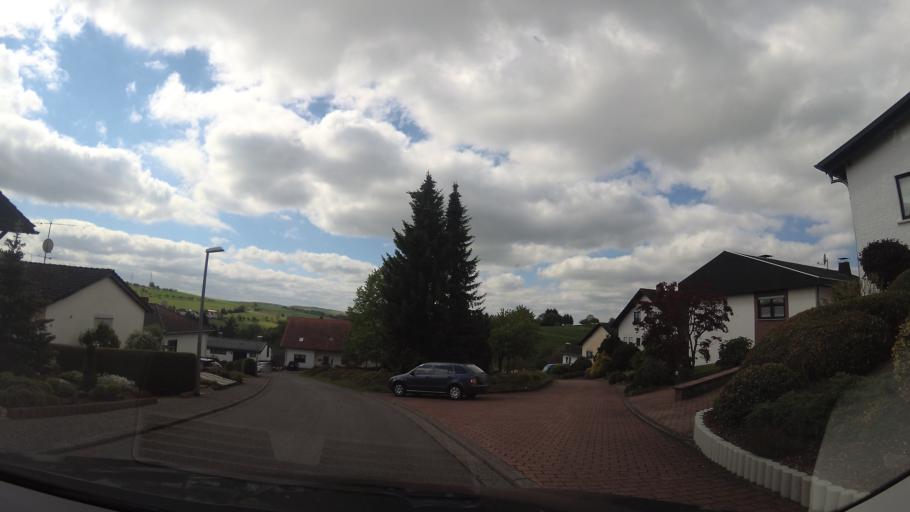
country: DE
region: Saarland
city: Eppelborn
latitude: 49.4331
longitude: 6.9442
